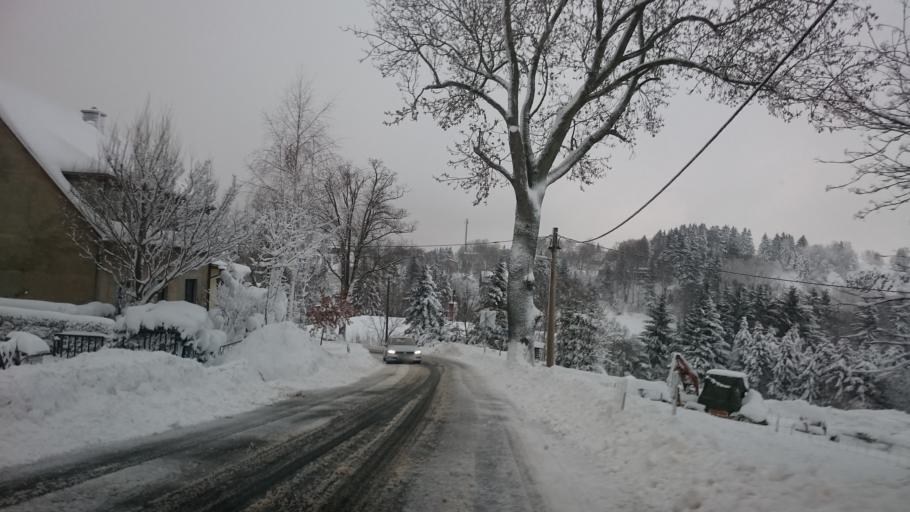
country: DE
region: Saxony
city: Geyer
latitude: 50.6201
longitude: 12.9226
